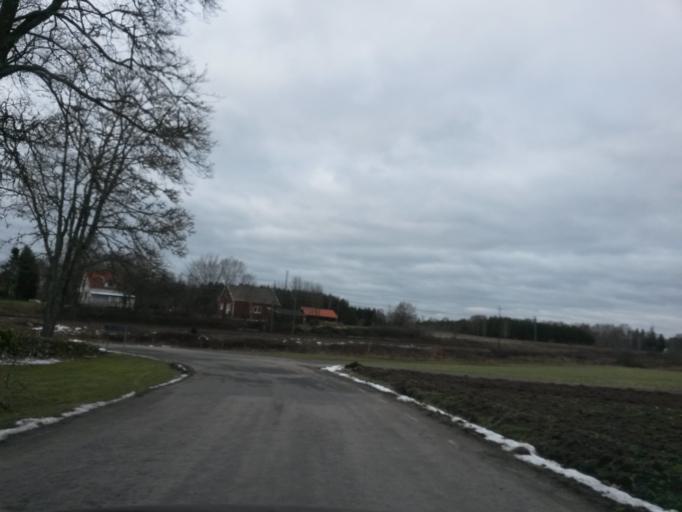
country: SE
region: Vaestra Goetaland
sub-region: Herrljunga Kommun
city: Herrljunga
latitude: 58.0632
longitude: 12.9525
